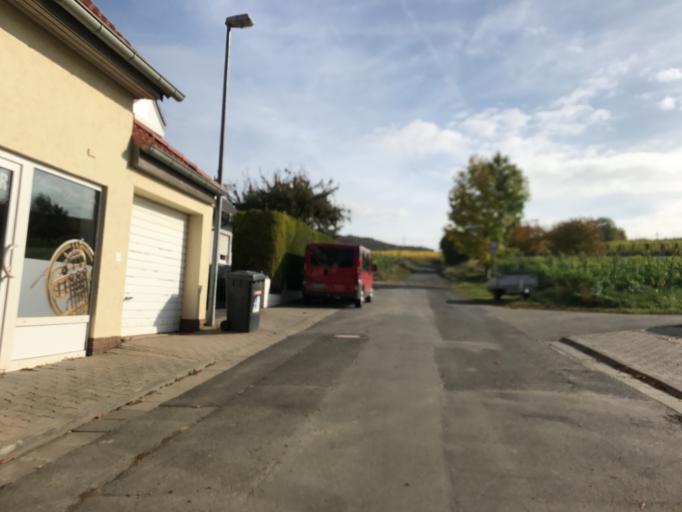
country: DE
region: Rheinland-Pfalz
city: Horrweiler
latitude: 49.9218
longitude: 7.9665
